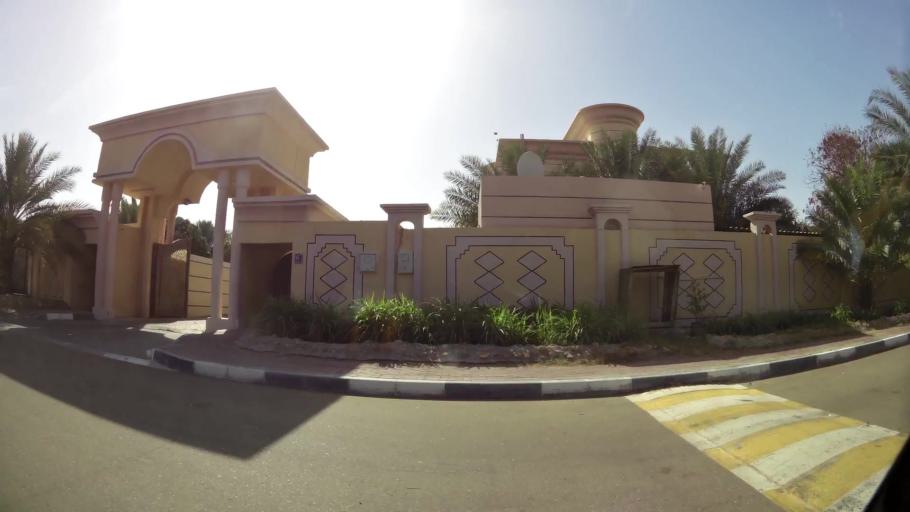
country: OM
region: Al Buraimi
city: Al Buraymi
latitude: 24.3276
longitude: 55.7969
